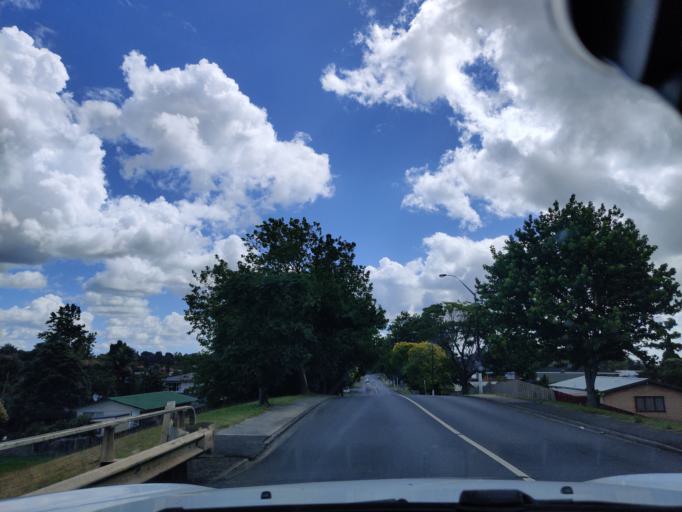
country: NZ
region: Auckland
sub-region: Auckland
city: Papakura
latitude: -37.0685
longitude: 174.9491
